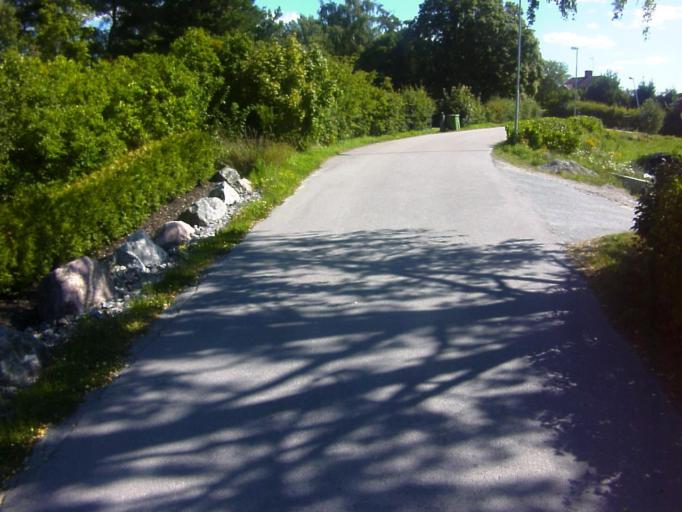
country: SE
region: Soedermanland
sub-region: Eskilstuna Kommun
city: Hallbybrunn
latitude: 59.3741
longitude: 16.4569
